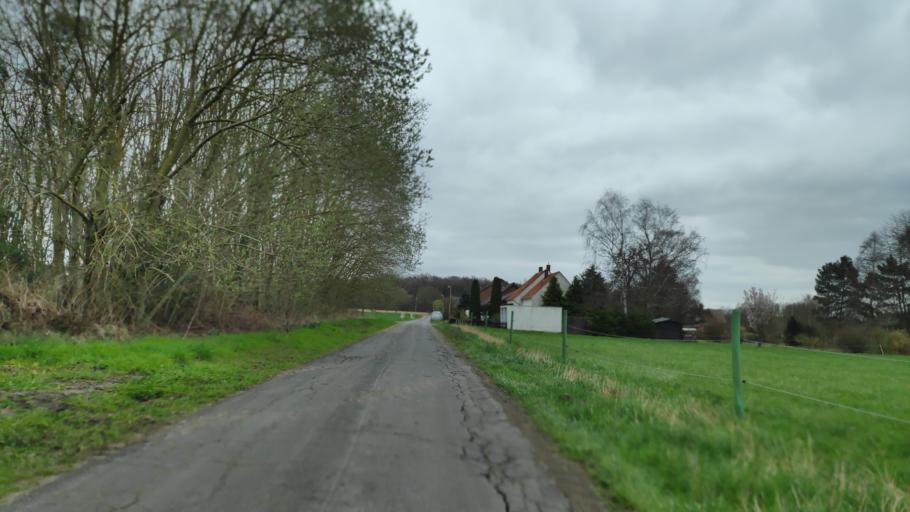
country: DE
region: North Rhine-Westphalia
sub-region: Regierungsbezirk Detmold
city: Petershagen
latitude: 52.3635
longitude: 8.8989
